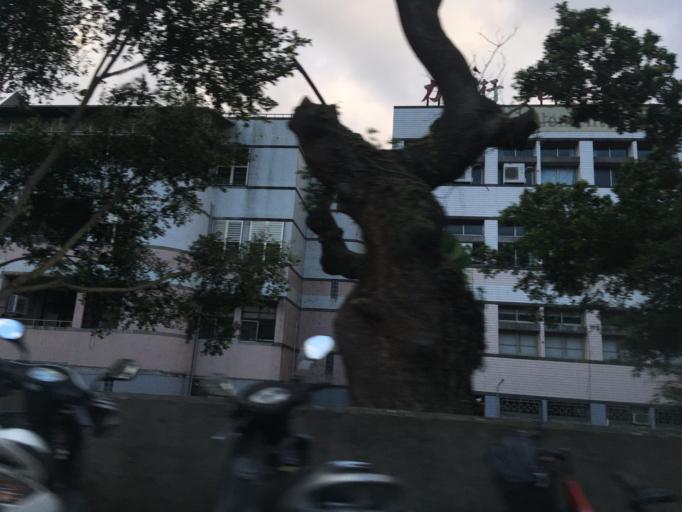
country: TW
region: Taiwan
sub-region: Yilan
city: Yilan
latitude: 24.7645
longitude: 121.7556
